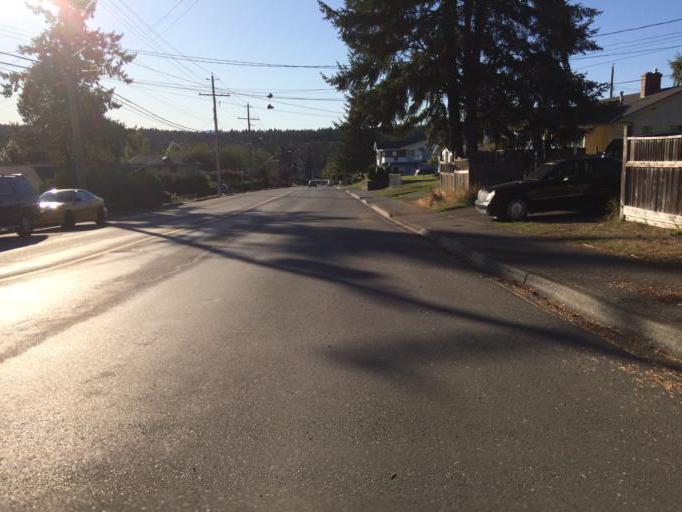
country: CA
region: British Columbia
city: Campbell River
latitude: 49.9843
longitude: -125.2329
